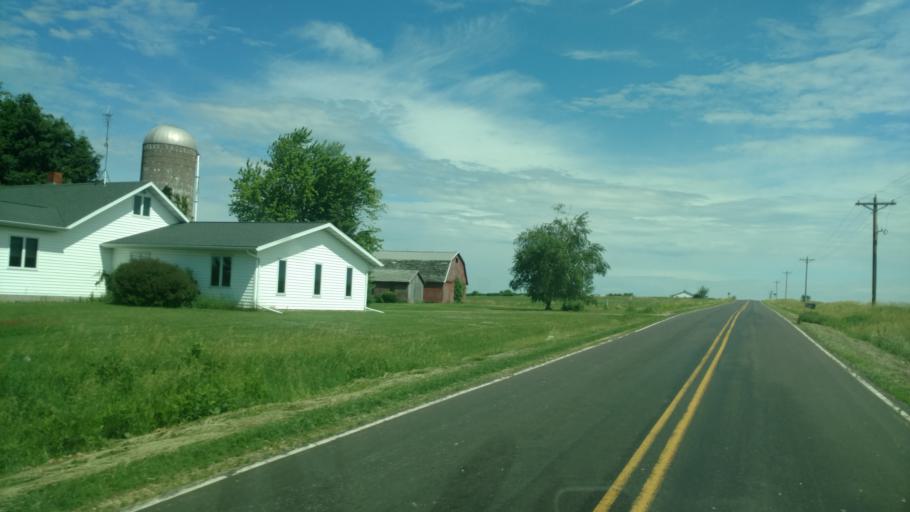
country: US
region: Wisconsin
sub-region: Vernon County
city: Hillsboro
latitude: 43.7235
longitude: -90.4479
